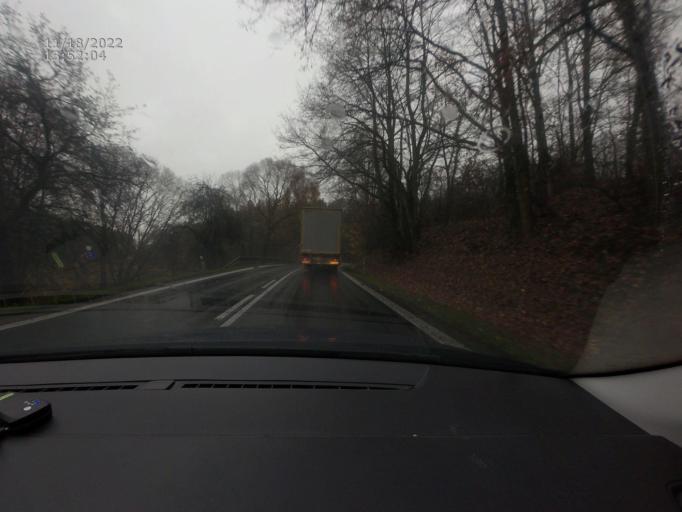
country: CZ
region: Jihocesky
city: Sedlice
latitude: 49.3966
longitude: 13.9097
